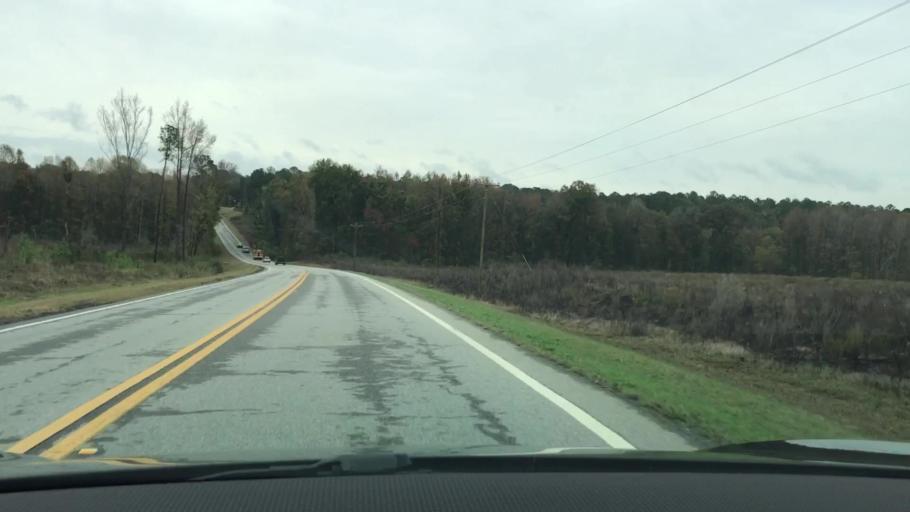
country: US
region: Georgia
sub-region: Greene County
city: Greensboro
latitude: 33.6122
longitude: -83.2078
